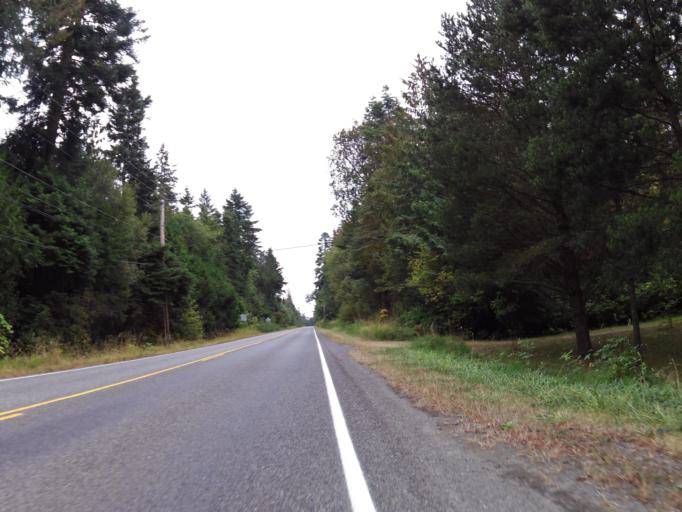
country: US
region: Washington
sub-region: Jefferson County
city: Port Ludlow
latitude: 47.9861
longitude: -122.7204
